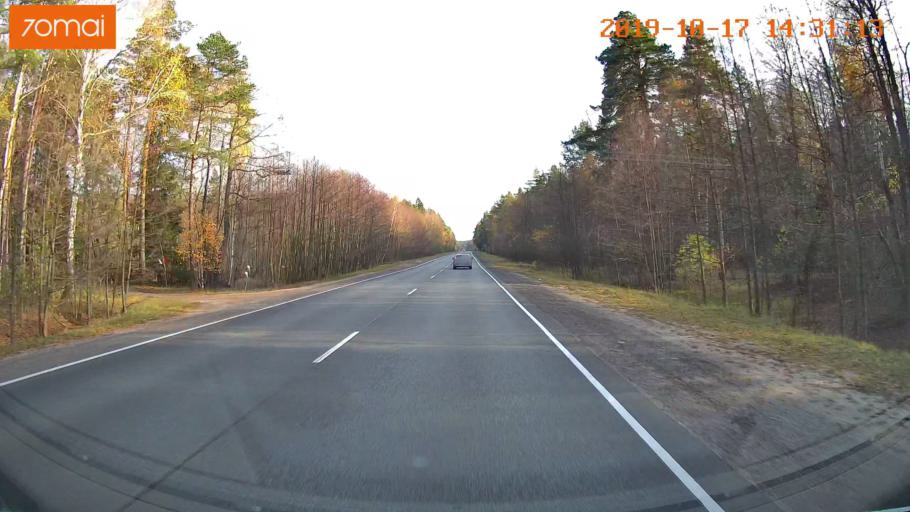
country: RU
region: Rjazan
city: Solotcha
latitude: 54.9387
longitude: 39.9579
